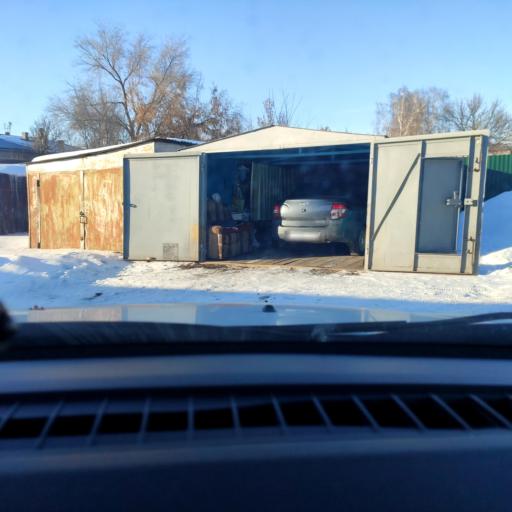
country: RU
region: Samara
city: Kurumoch
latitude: 53.4872
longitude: 50.0363
